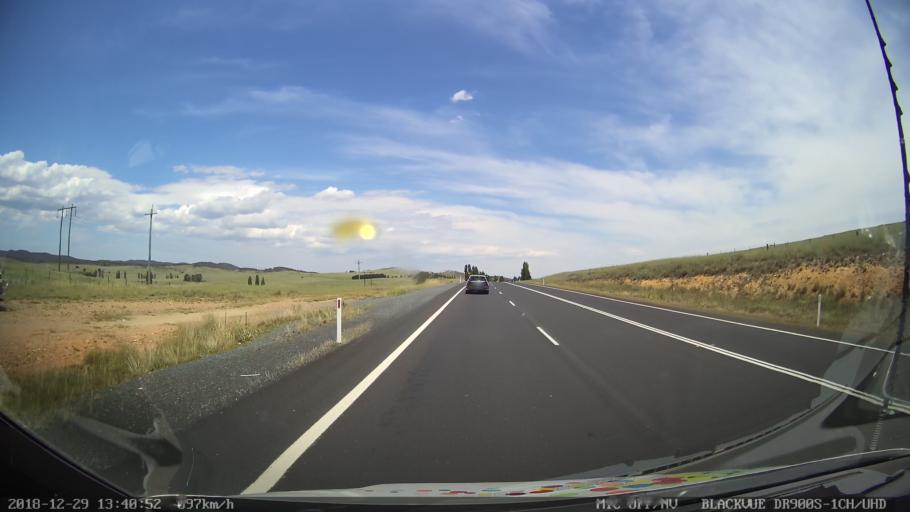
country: AU
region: New South Wales
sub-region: Cooma-Monaro
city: Cooma
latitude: -36.0335
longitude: 149.1545
